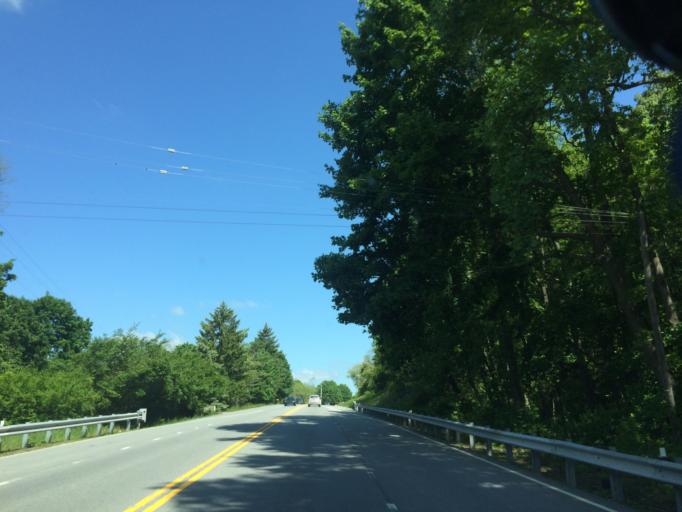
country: US
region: Maryland
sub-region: Carroll County
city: Manchester
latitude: 39.7049
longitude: -76.9125
